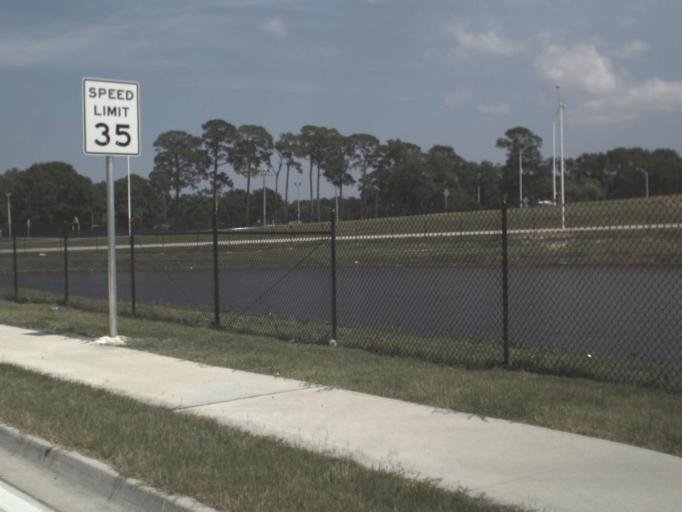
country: US
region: Florida
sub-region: Duval County
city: Jacksonville
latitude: 30.3574
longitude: -81.6385
